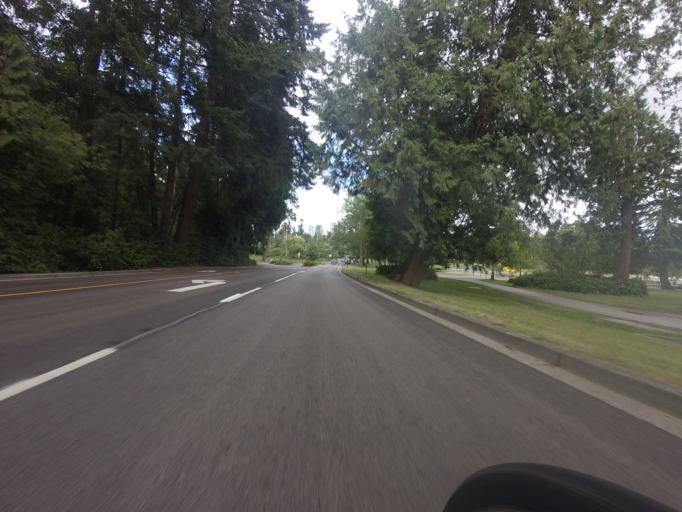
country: CA
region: British Columbia
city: West End
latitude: 49.2959
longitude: -123.1503
